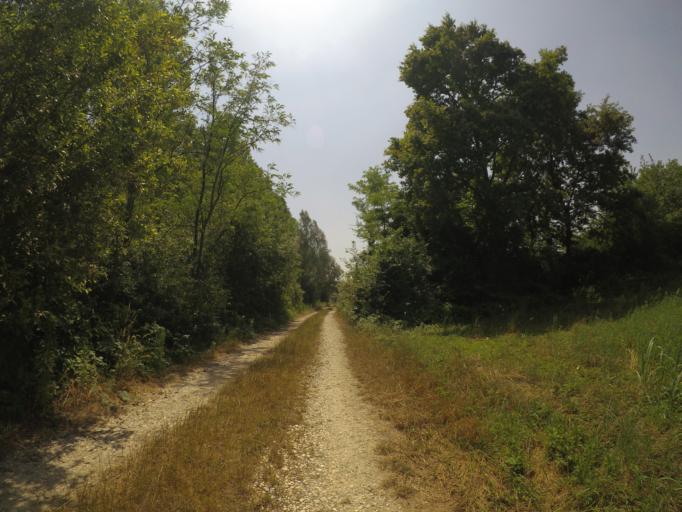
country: IT
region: Friuli Venezia Giulia
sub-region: Provincia di Udine
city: Bertiolo
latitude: 45.9238
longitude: 13.0534
